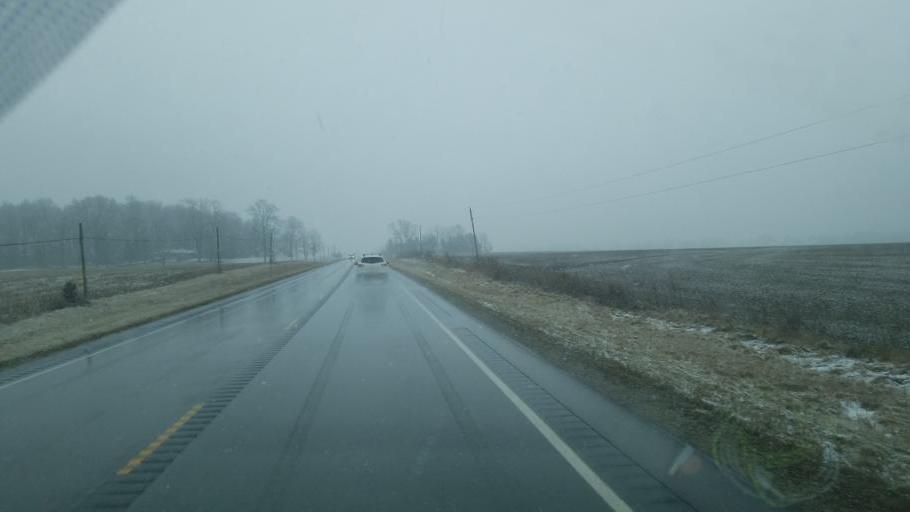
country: US
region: Indiana
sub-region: Grant County
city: Sweetser
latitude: 40.6368
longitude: -85.7085
